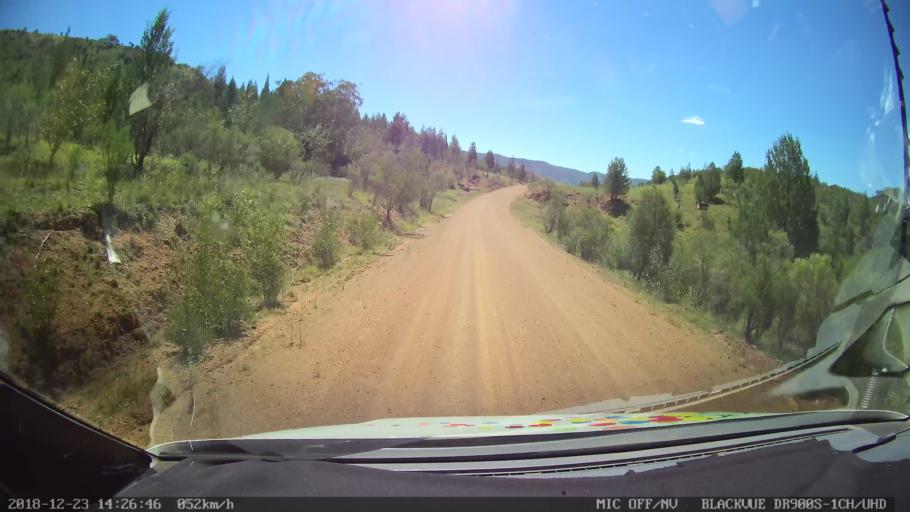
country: AU
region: New South Wales
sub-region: Tamworth Municipality
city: Manilla
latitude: -30.6213
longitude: 150.9512
